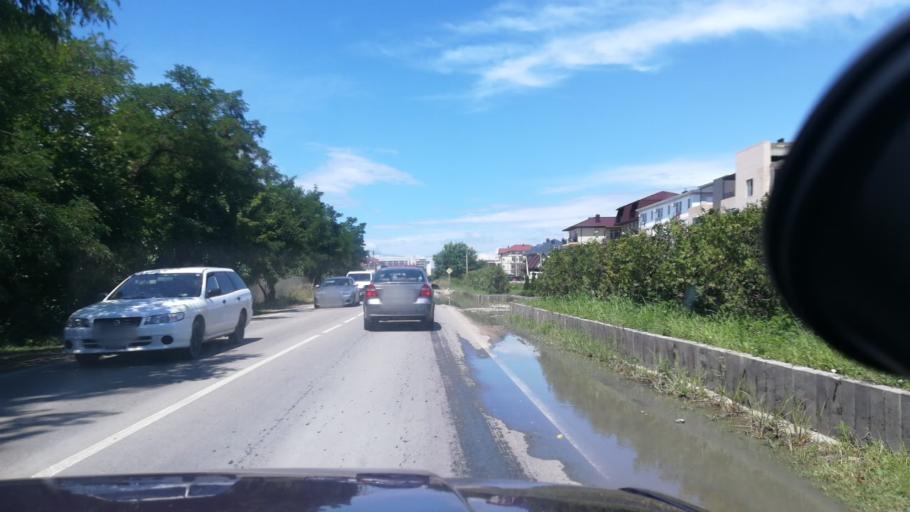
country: RU
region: Krasnodarskiy
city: Vityazevo
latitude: 44.9596
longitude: 37.2960
